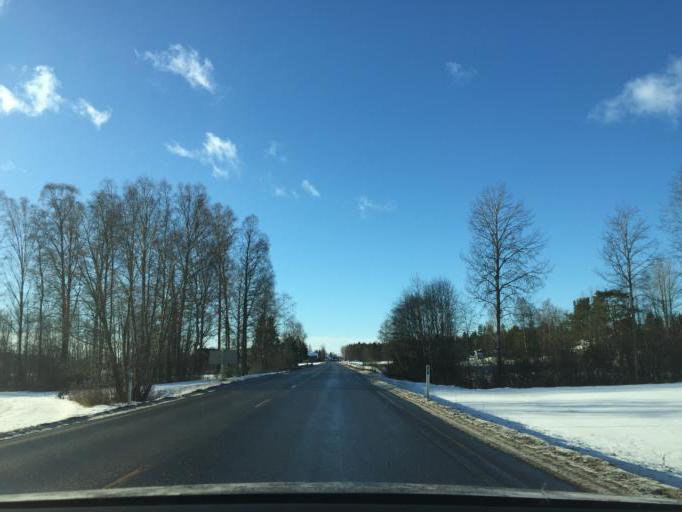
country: NO
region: Hedmark
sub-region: Sor-Odal
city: Skarnes
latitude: 60.2138
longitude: 11.6275
